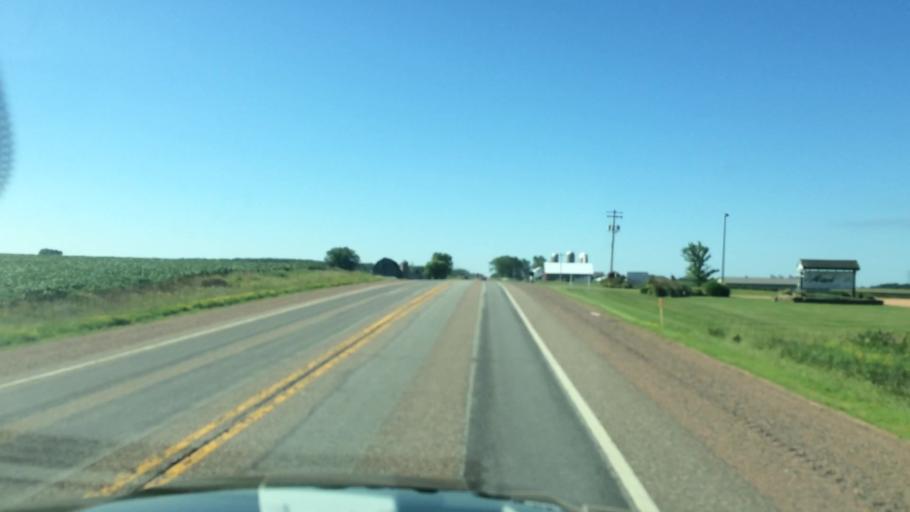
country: US
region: Wisconsin
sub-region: Marathon County
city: Stratford
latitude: 44.9069
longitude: -90.0786
